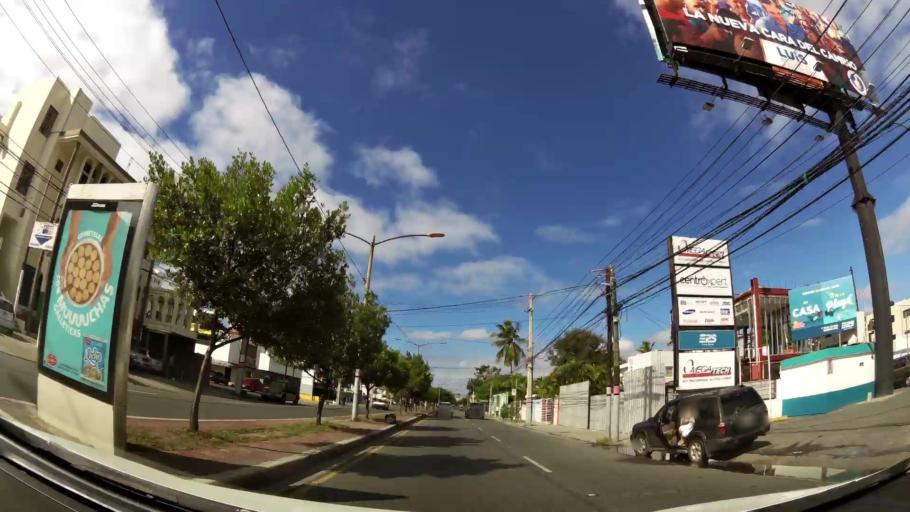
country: DO
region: Nacional
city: Bella Vista
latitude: 18.4575
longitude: -69.9391
